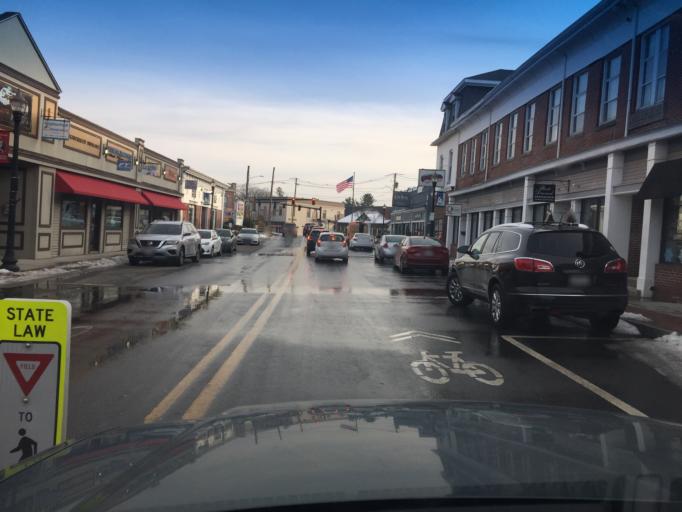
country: US
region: Massachusetts
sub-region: Norfolk County
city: Franklin
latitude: 42.0833
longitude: -71.3977
